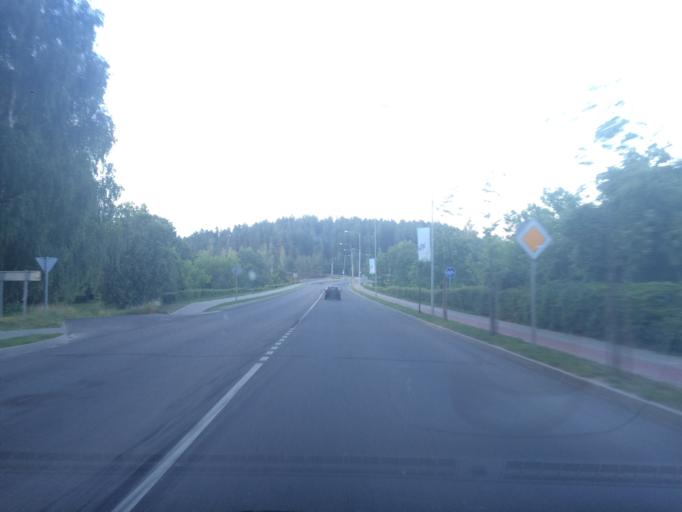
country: LT
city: Zarasai
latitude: 55.7267
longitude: 26.2457
